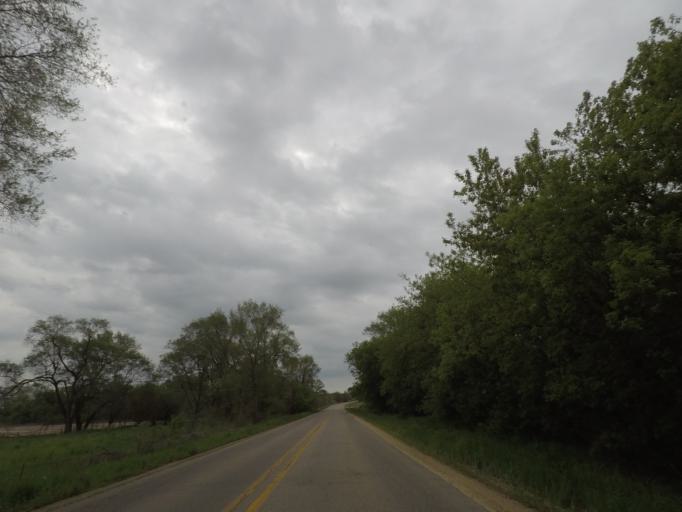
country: US
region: Illinois
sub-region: Winnebago County
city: Roscoe
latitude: 42.4517
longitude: -88.9920
